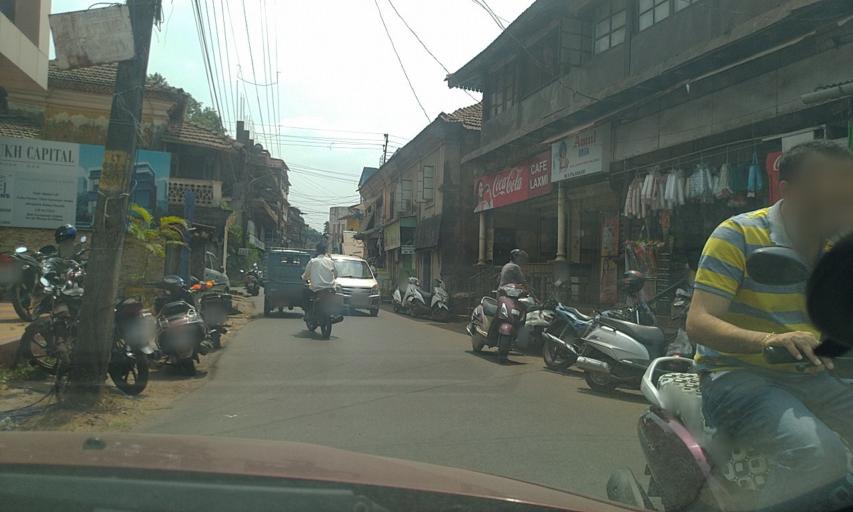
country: IN
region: Goa
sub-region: North Goa
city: Mapuca
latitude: 15.5915
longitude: 73.8102
